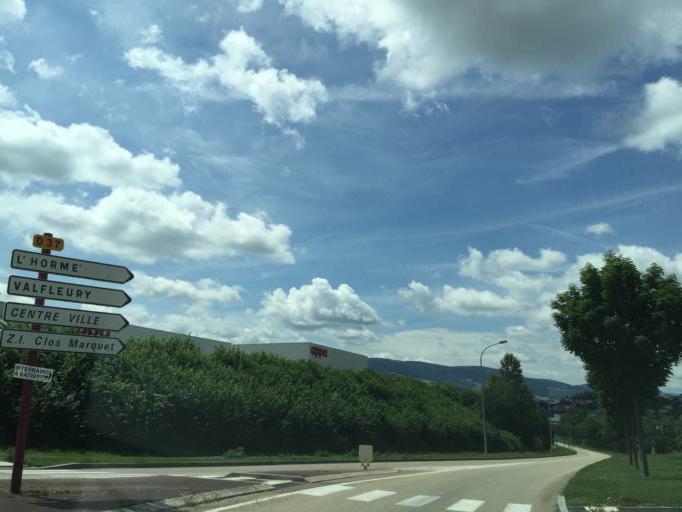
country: FR
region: Rhone-Alpes
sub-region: Departement de la Loire
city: Saint-Chamond
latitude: 45.4902
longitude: 4.5212
